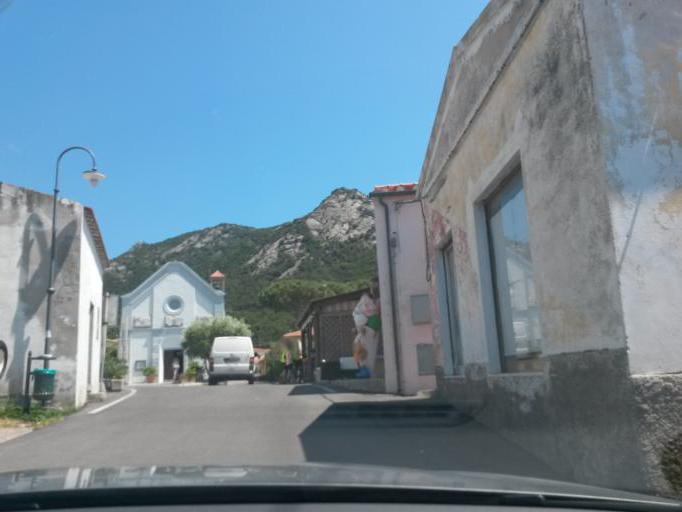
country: IT
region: Tuscany
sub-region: Provincia di Livorno
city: Marciana
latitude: 42.7487
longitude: 10.1205
